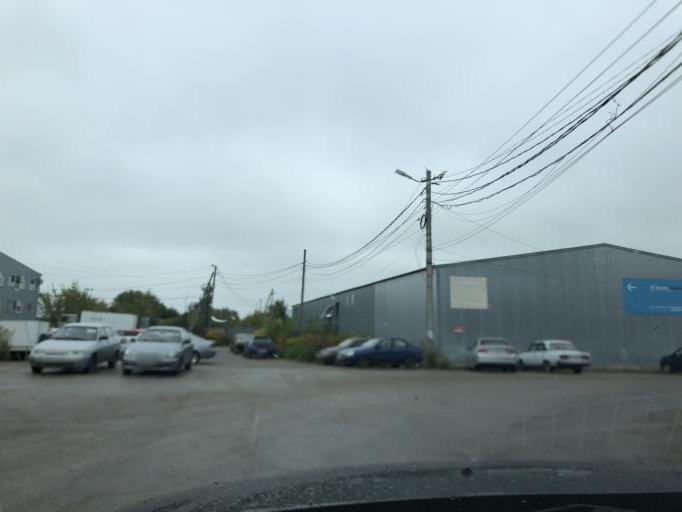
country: RU
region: Tula
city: Kosaya Gora
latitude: 54.1861
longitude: 37.5231
